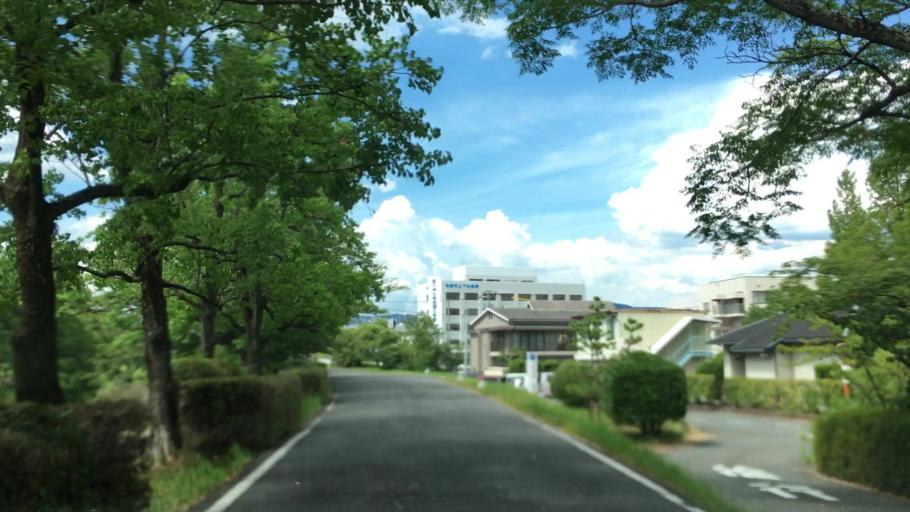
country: JP
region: Saga Prefecture
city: Saga-shi
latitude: 33.2715
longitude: 130.2825
